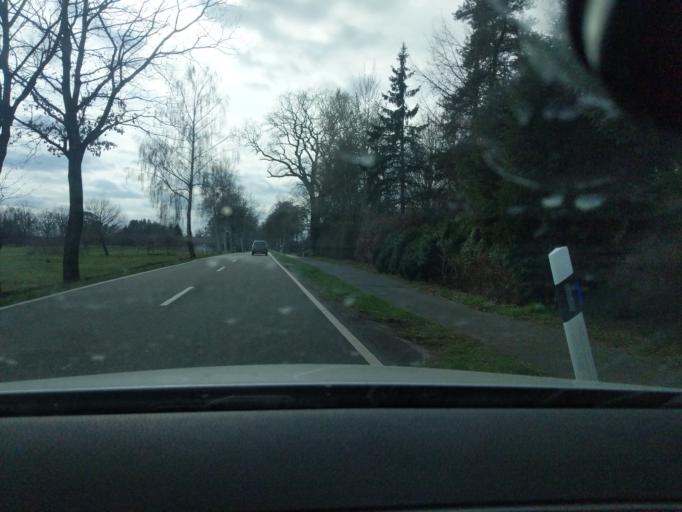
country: DE
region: Lower Saxony
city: Himmelpforten
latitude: 53.6360
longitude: 9.3256
